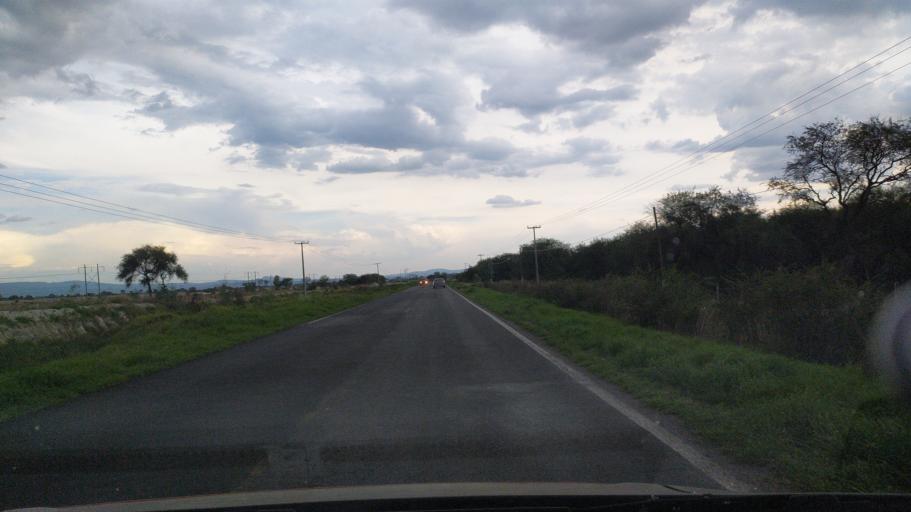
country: MX
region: Guanajuato
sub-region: San Francisco del Rincon
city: San Ignacio de Hidalgo
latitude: 20.8415
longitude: -101.8978
